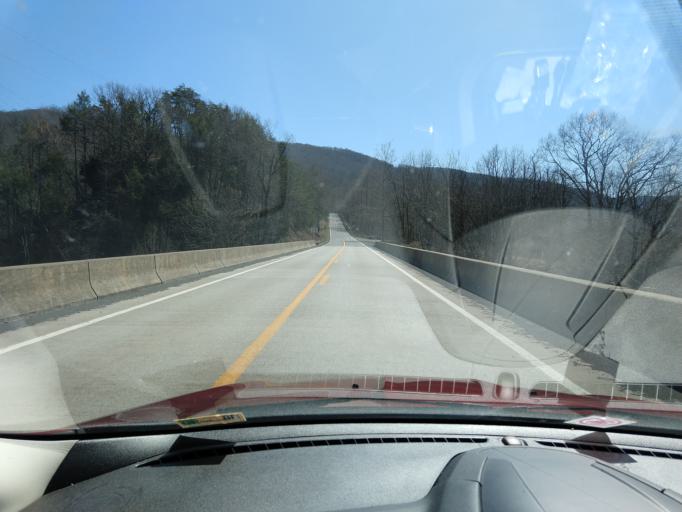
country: US
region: West Virginia
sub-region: Summers County
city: Hinton
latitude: 37.7698
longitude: -80.8918
